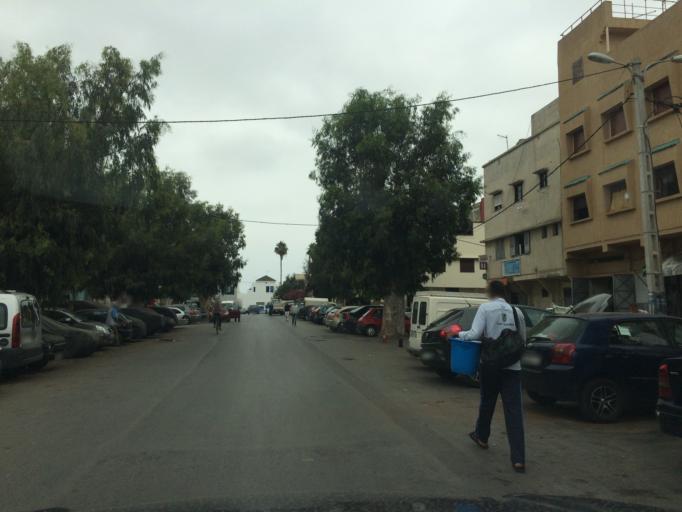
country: MA
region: Rabat-Sale-Zemmour-Zaer
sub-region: Rabat
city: Rabat
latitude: 33.9825
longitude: -6.8250
